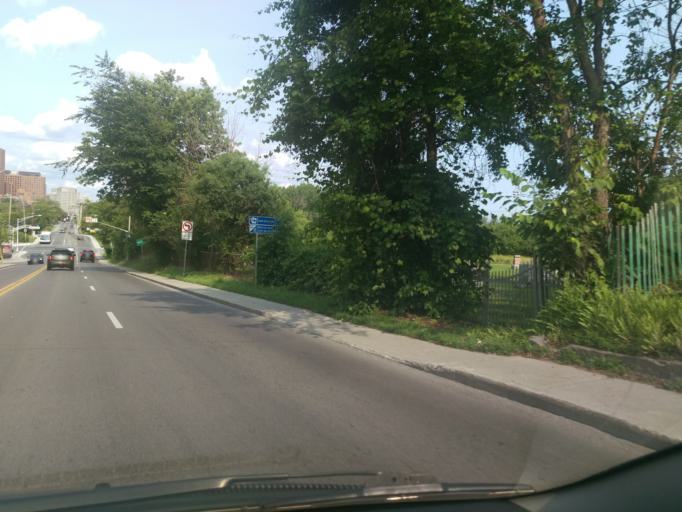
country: CA
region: Ontario
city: Ottawa
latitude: 45.4231
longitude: -75.7358
